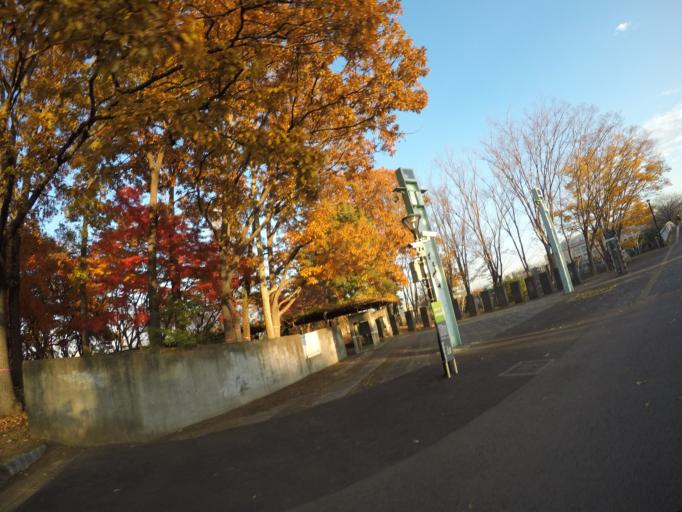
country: JP
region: Ibaraki
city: Naka
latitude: 36.0898
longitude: 140.1072
